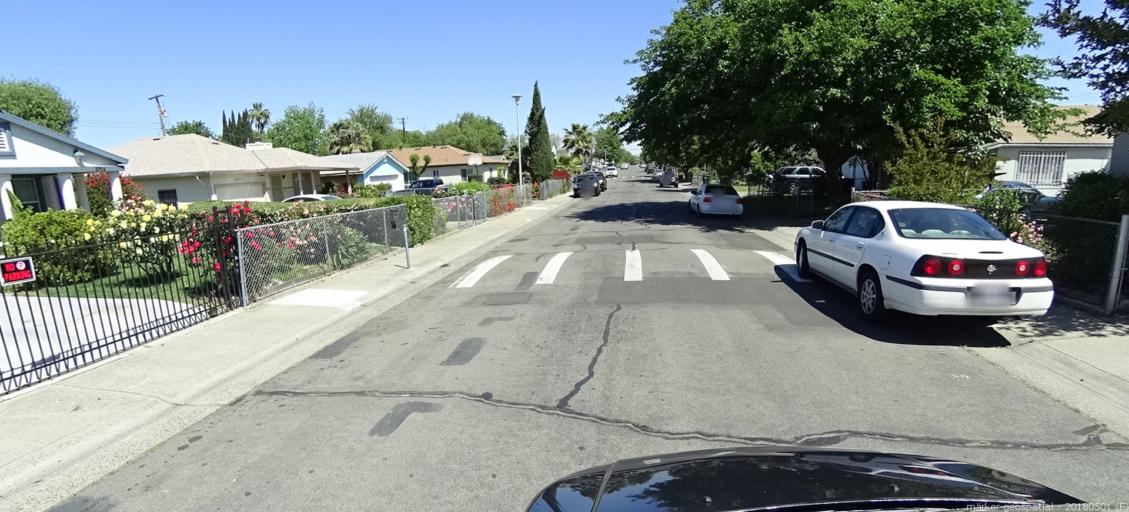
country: US
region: California
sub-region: Sacramento County
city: Rio Linda
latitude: 38.6351
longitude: -121.4439
